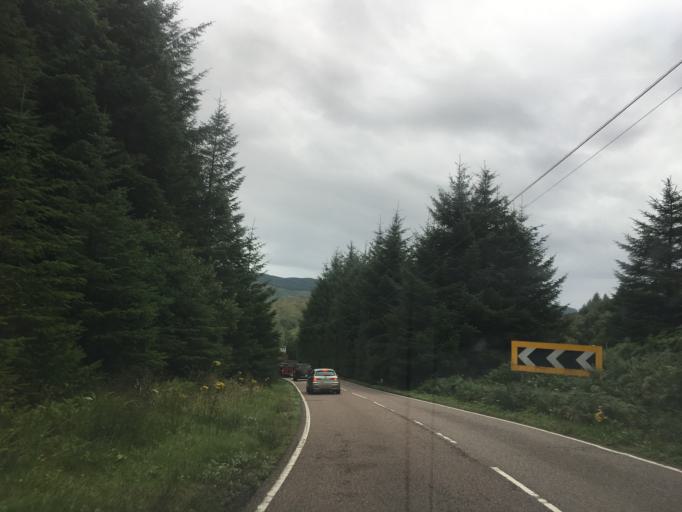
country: GB
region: Scotland
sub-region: Argyll and Bute
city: Oban
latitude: 56.2802
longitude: -5.4839
